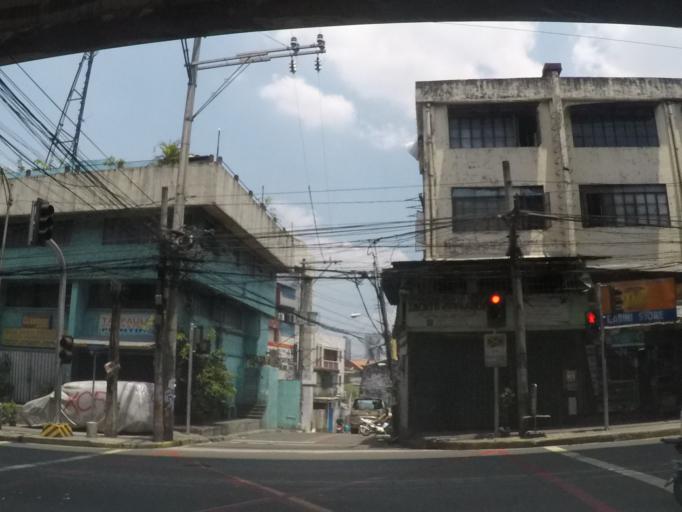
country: PH
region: Metro Manila
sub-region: San Juan
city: San Juan
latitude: 14.6099
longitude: 121.0245
